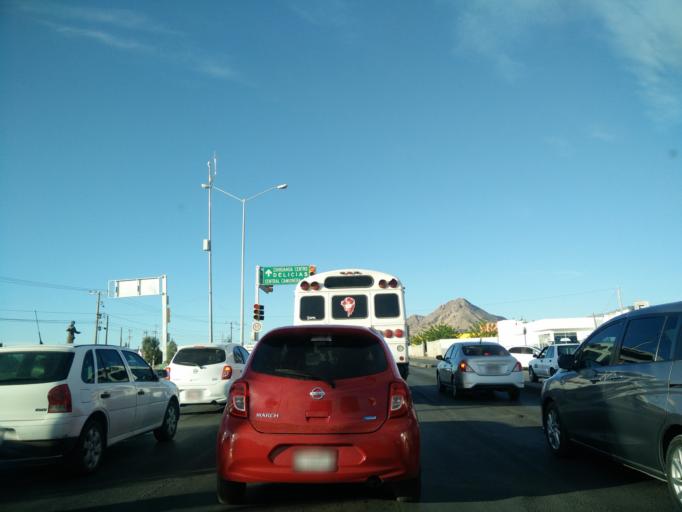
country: MX
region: Chihuahua
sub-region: Chihuahua
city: Chihuahua
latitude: 28.6277
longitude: -106.0241
